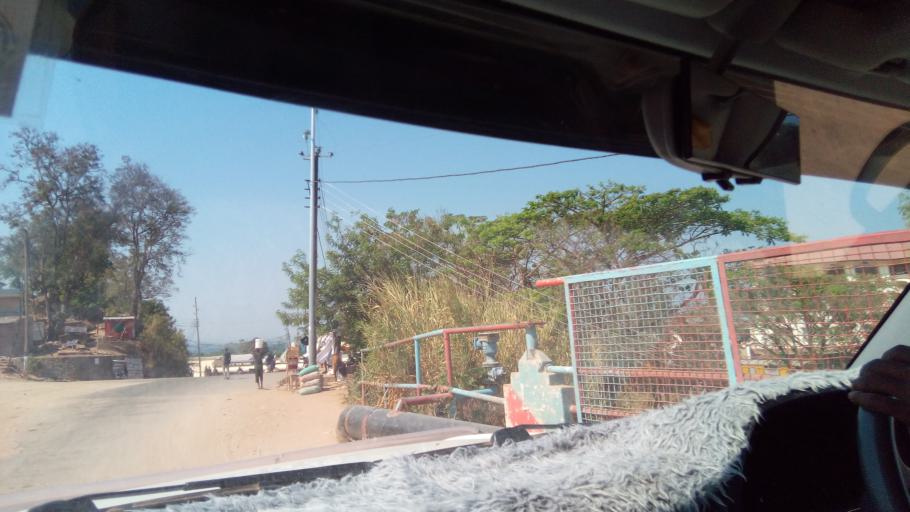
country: CD
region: Katanga
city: Kalemie
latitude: -5.9472
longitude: 29.1966
